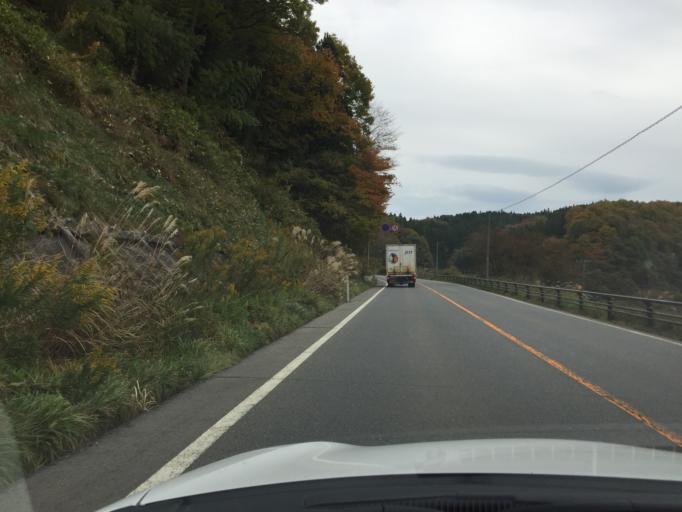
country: JP
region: Fukushima
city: Ishikawa
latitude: 37.2141
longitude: 140.6029
